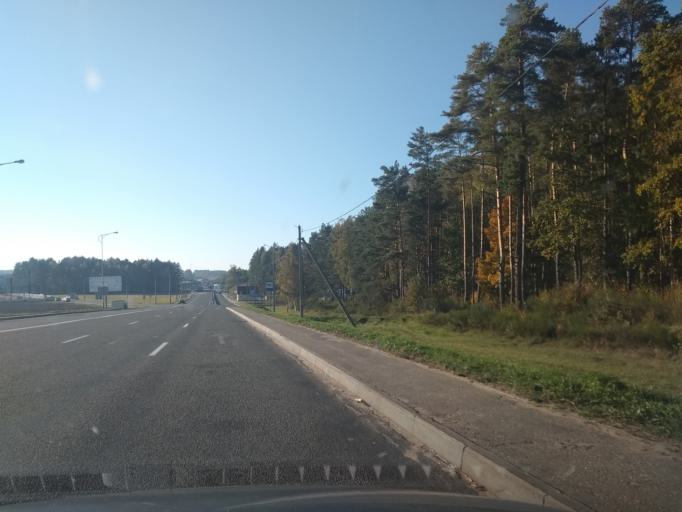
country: BY
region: Grodnenskaya
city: Vyalikaya Byerastavitsa
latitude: 53.1215
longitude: 23.9098
